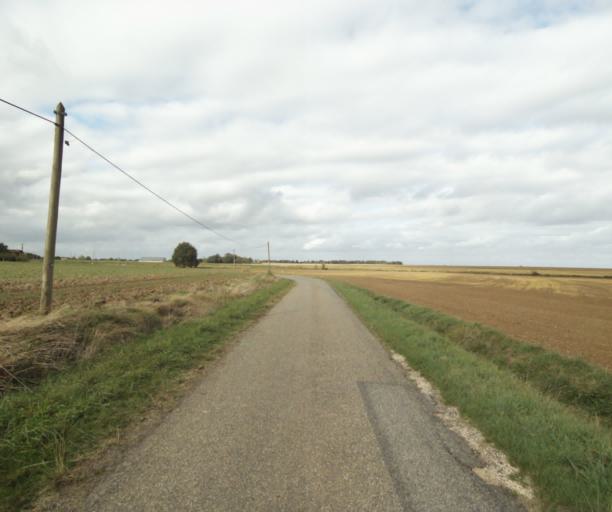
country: FR
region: Midi-Pyrenees
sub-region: Departement du Tarn-et-Garonne
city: Beaumont-de-Lomagne
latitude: 43.8822
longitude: 1.0852
